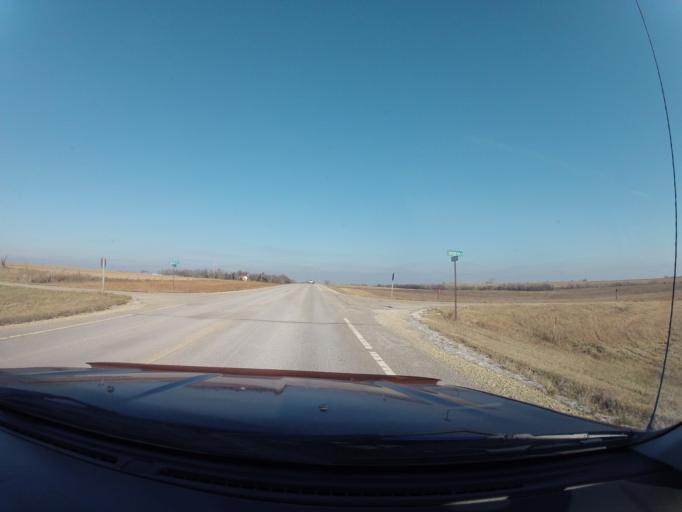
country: US
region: Kansas
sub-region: Marshall County
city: Blue Rapids
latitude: 39.5515
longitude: -96.7553
